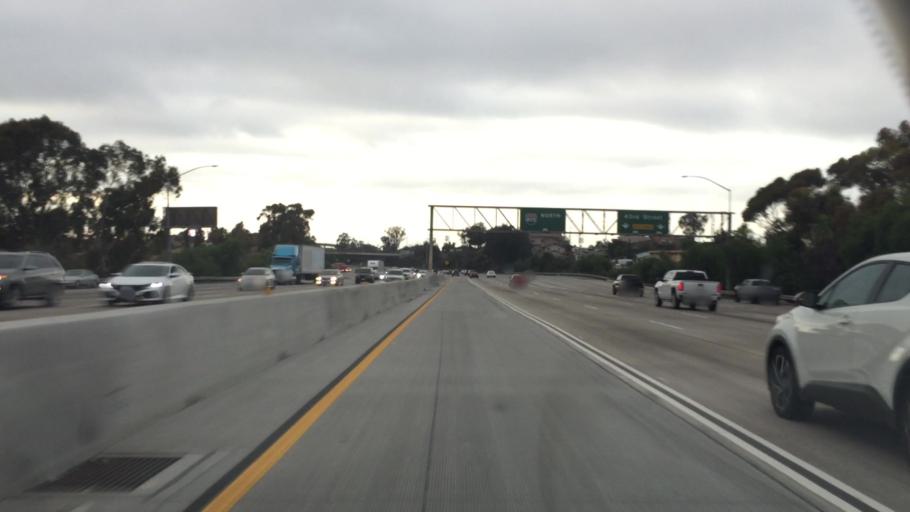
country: US
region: California
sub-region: San Diego County
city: National City
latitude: 32.6804
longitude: -117.0863
